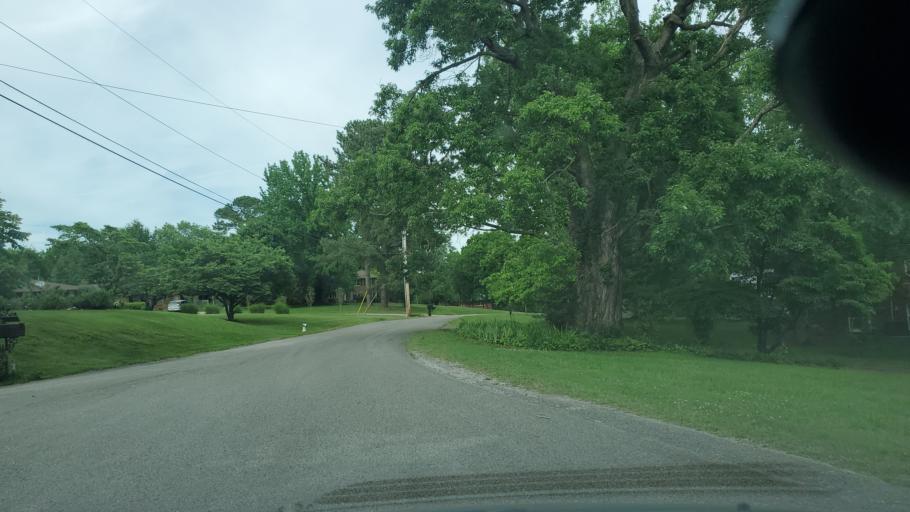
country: US
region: Tennessee
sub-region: Davidson County
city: Lakewood
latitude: 36.2159
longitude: -86.6861
